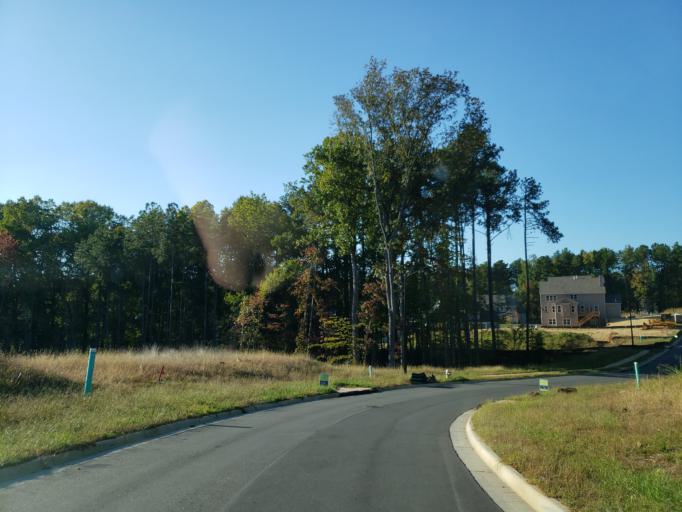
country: US
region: Georgia
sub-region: Cobb County
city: Kennesaw
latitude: 34.0021
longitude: -84.6736
